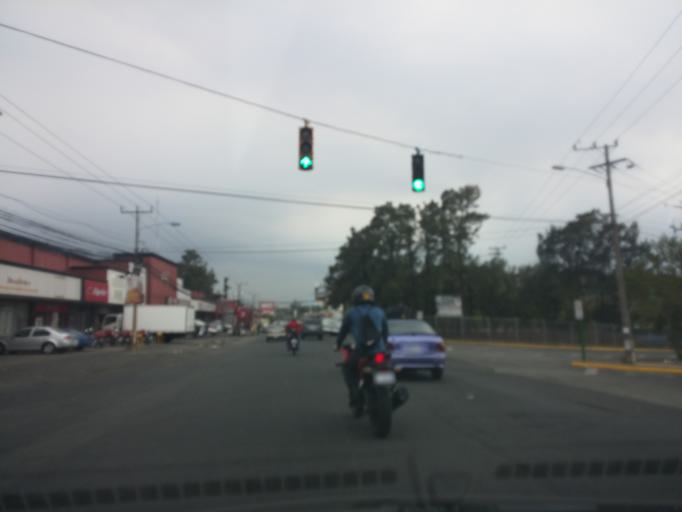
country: CR
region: Heredia
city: Llorente
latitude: 9.9815
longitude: -84.1521
